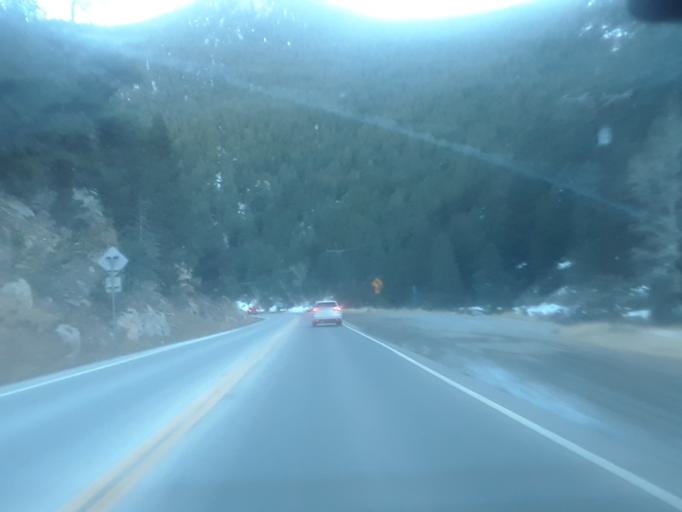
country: US
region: Colorado
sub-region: Clear Creek County
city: Idaho Springs
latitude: 39.7385
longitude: -105.4223
